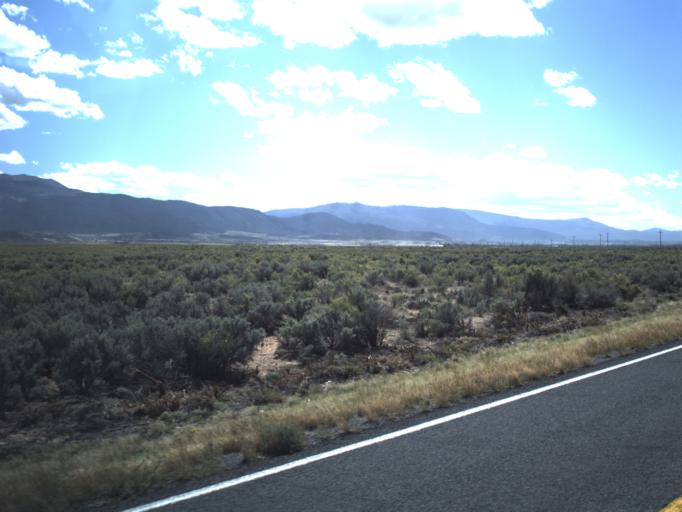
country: US
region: Utah
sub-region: Iron County
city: Enoch
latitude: 37.8371
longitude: -113.0491
